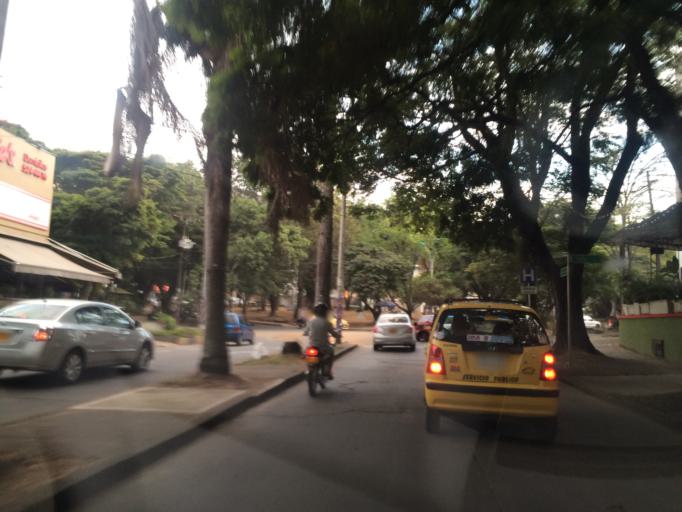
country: CO
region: Valle del Cauca
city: Cali
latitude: 3.4349
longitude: -76.5448
